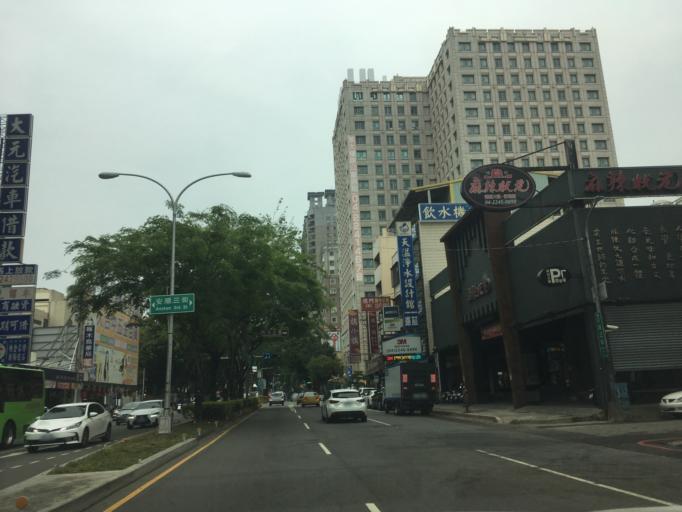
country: TW
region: Taiwan
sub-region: Taichung City
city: Taichung
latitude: 24.1736
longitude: 120.6857
